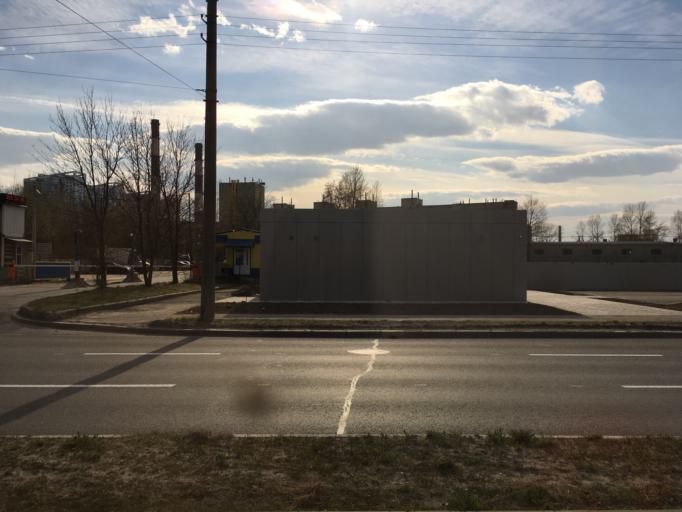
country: RU
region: St.-Petersburg
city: Obukhovo
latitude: 59.8964
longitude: 30.4612
